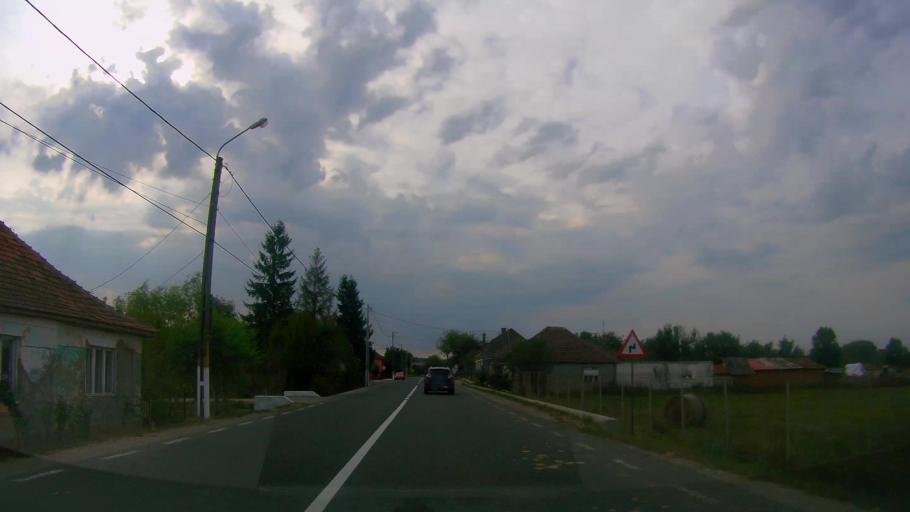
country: RO
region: Satu Mare
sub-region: Oras Ardud
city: Ardud
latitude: 47.5873
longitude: 22.8843
